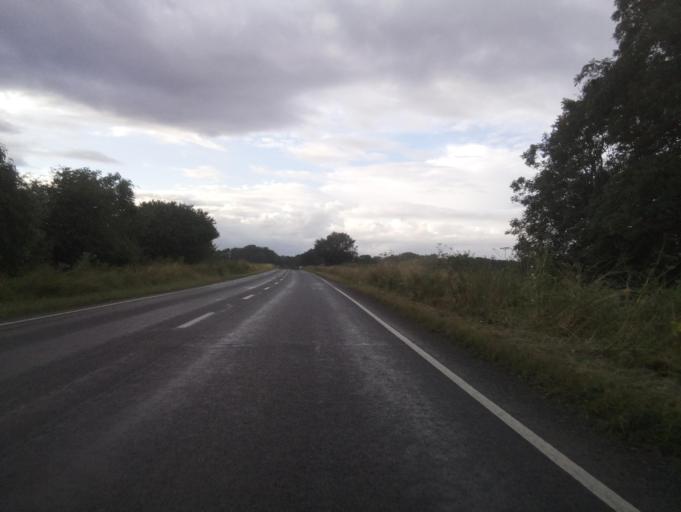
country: GB
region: England
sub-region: Oxfordshire
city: Woodstock
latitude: 51.8941
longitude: -1.3271
